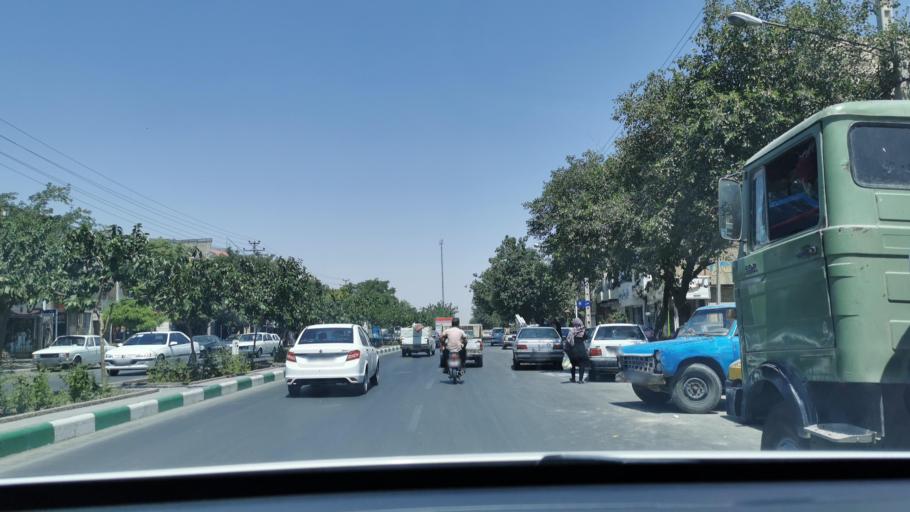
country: IR
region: Razavi Khorasan
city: Mashhad
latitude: 36.3417
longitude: 59.6251
